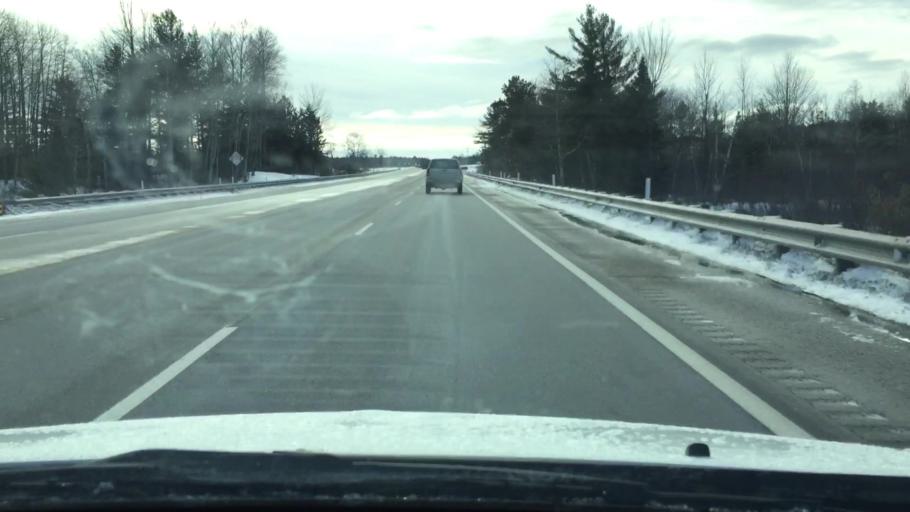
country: US
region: Michigan
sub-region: Kalkaska County
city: Kalkaska
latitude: 44.6772
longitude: -85.2322
